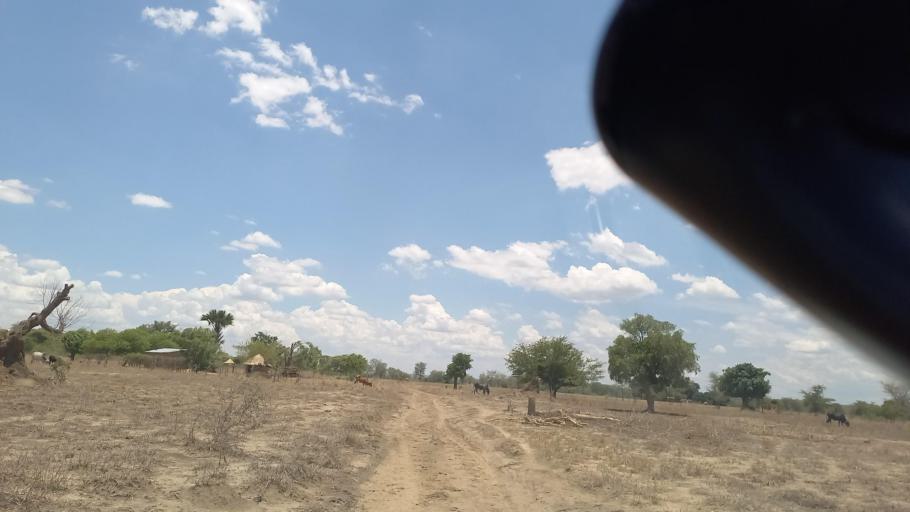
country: ZM
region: Southern
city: Mazabuka
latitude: -16.1269
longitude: 27.7789
